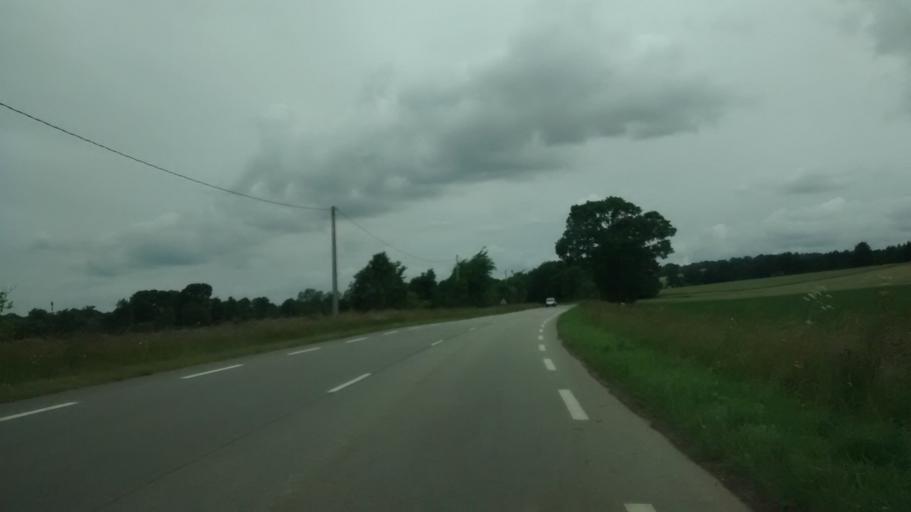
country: FR
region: Brittany
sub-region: Departement du Morbihan
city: Malestroit
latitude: 47.8077
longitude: -2.3329
